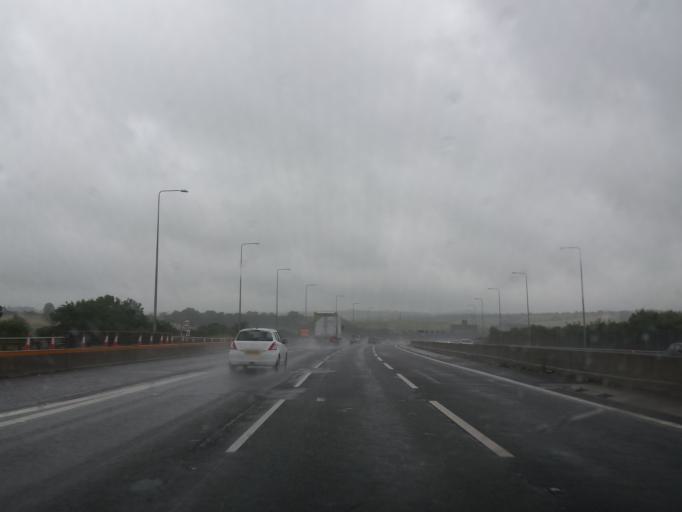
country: GB
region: England
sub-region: Derbyshire
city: Pinxton
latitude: 53.0979
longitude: -1.3165
